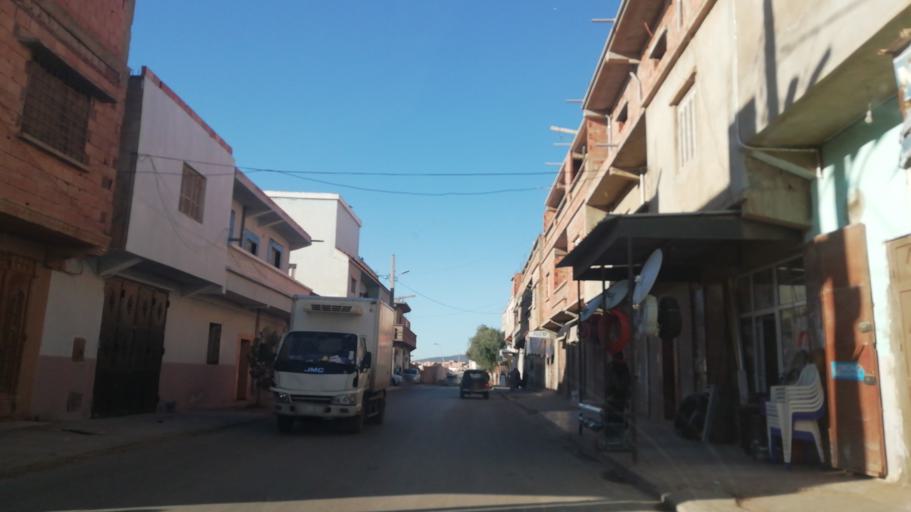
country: DZ
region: Oran
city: Sidi ech Chahmi
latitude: 35.6936
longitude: -0.4941
